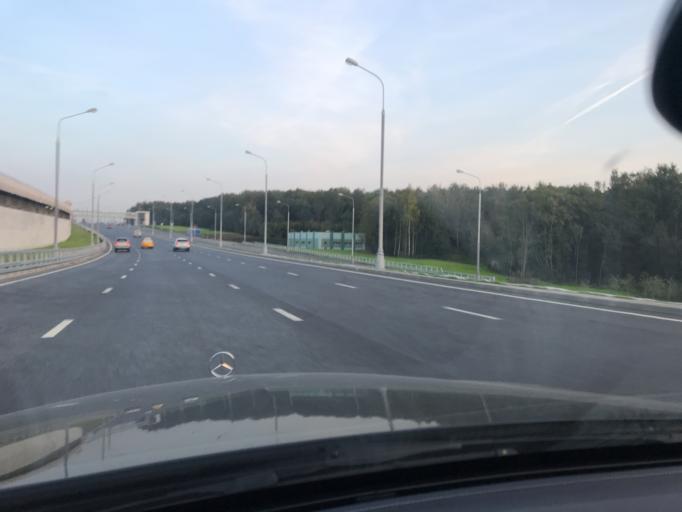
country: RU
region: Moskovskaya
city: Mosrentgen
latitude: 55.5889
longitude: 37.4267
